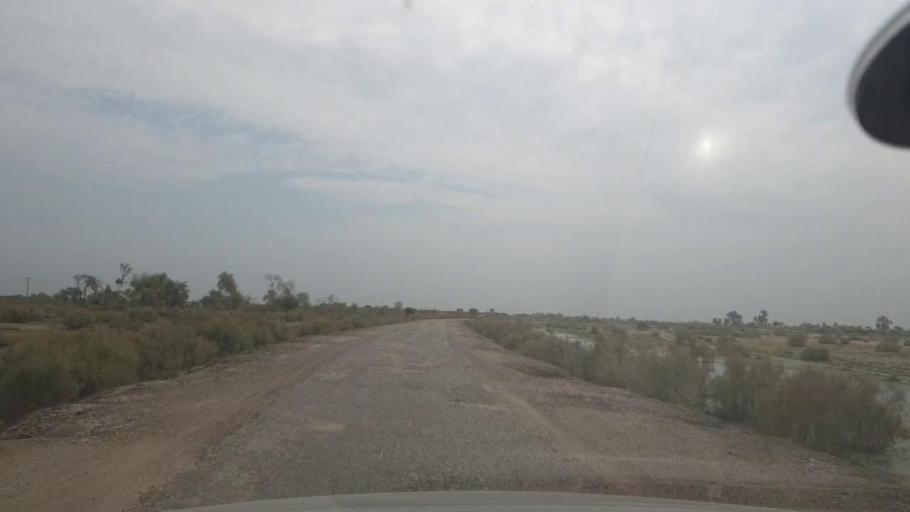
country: PK
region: Balochistan
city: Mehrabpur
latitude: 28.0565
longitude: 68.1377
